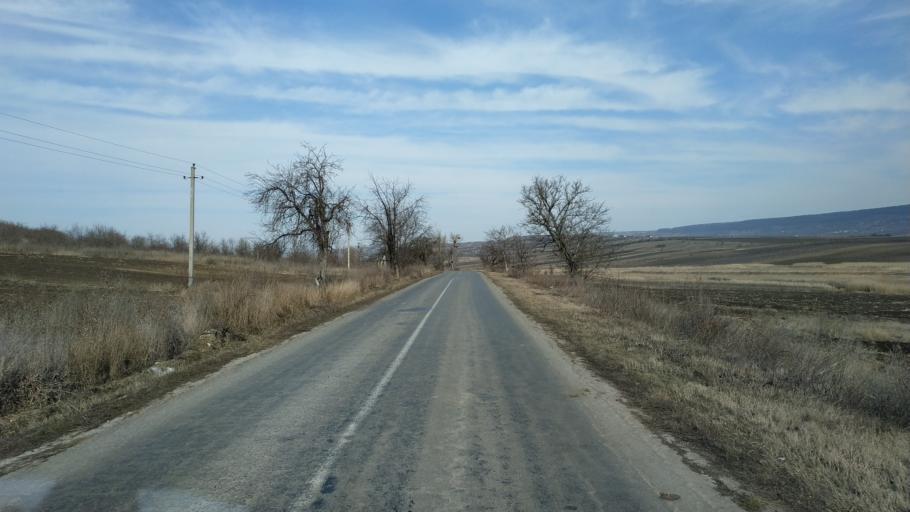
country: MD
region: Nisporeni
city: Nisporeni
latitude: 47.1290
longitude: 28.1213
